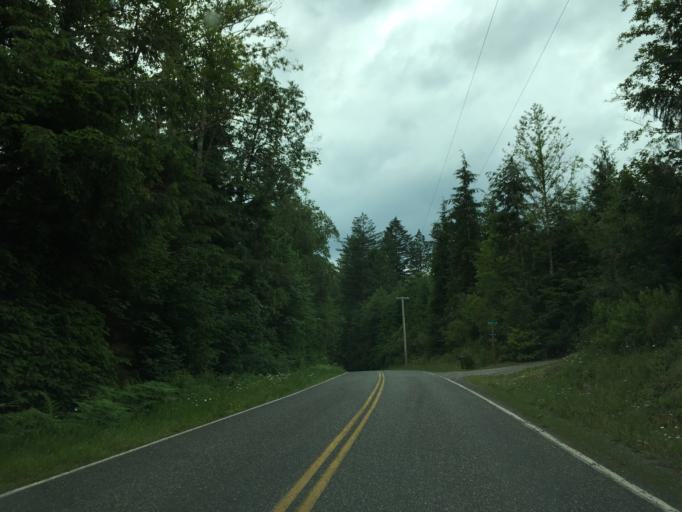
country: US
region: Washington
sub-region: Whatcom County
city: Peaceful Valley
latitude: 48.9889
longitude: -122.1058
